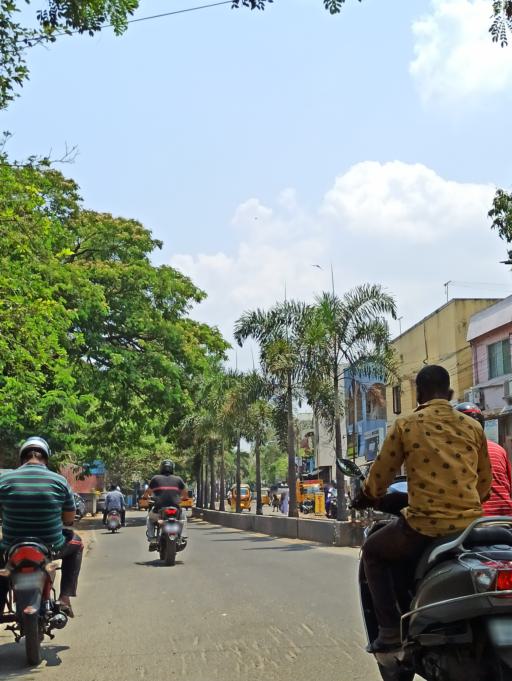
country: IN
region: Tamil Nadu
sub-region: Chennai
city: Chetput
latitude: 13.0915
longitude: 80.2318
